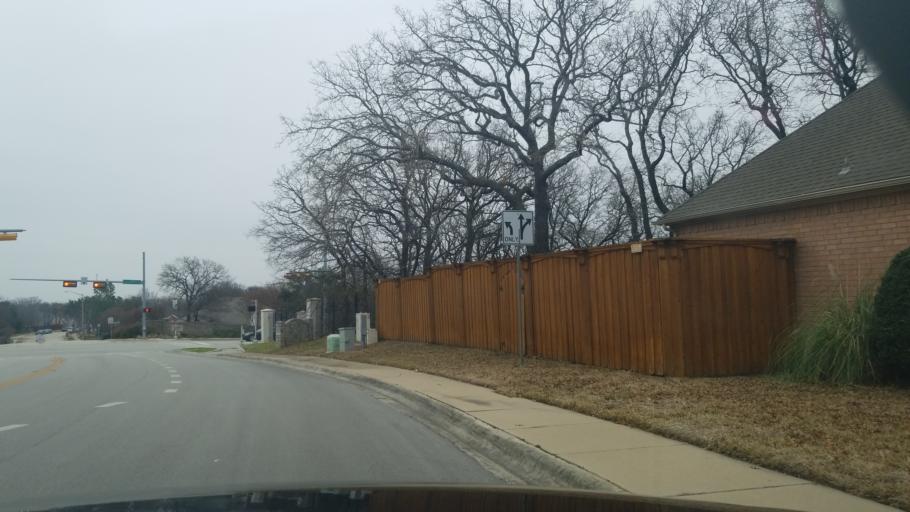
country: US
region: Texas
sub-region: Denton County
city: Denton
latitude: 33.1816
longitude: -97.1109
